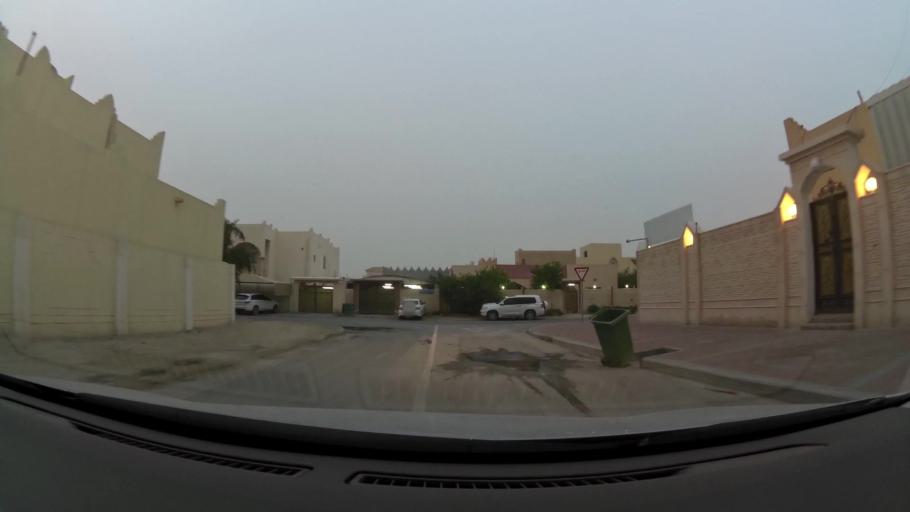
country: QA
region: Baladiyat ad Dawhah
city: Doha
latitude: 25.2287
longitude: 51.4947
